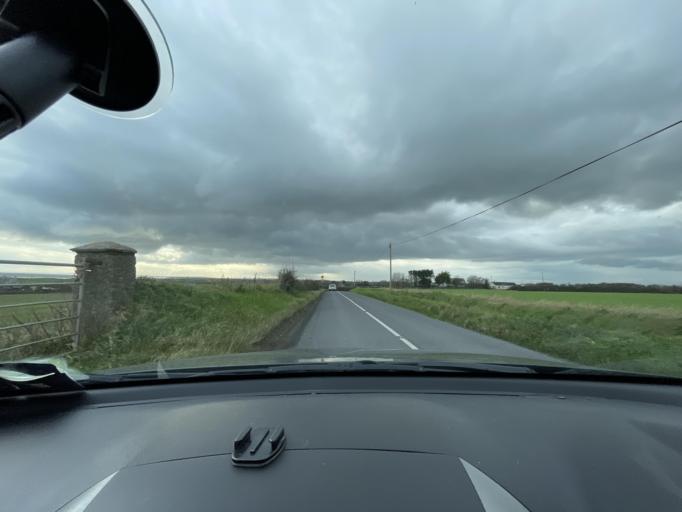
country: IE
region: Leinster
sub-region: Lu
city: Termonfeckin
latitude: 53.7725
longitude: -6.2493
